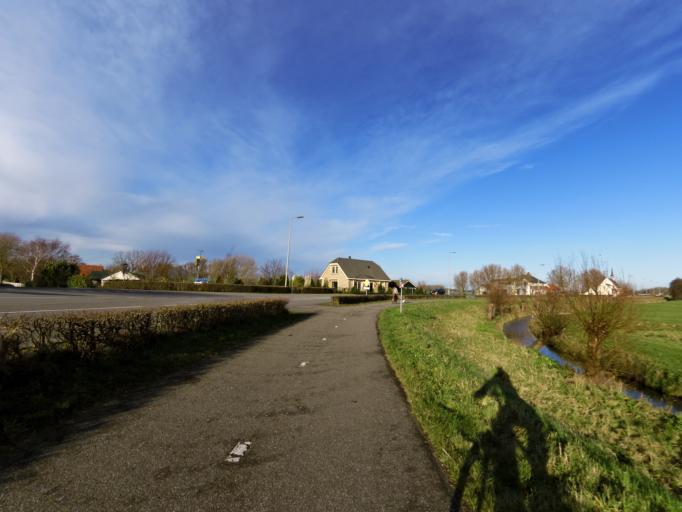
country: NL
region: South Holland
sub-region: Gemeente Hellevoetsluis
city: Nieuw-Helvoet
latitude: 51.8785
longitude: 4.0662
